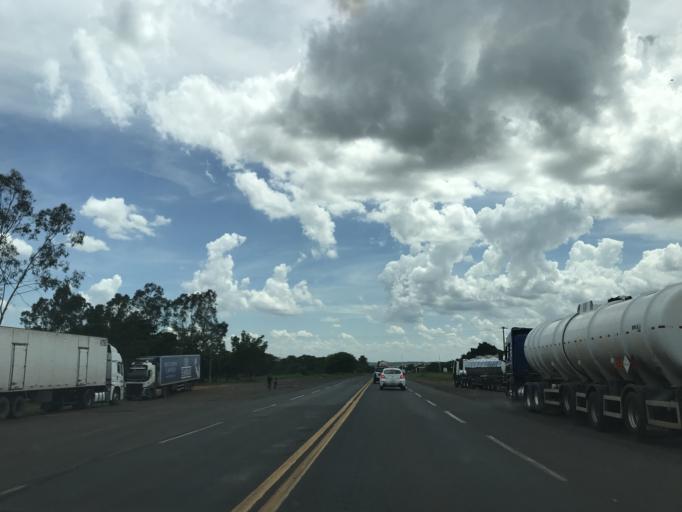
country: BR
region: Sao Paulo
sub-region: Nova Granada
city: Nova Granada
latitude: -20.2854
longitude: -49.1977
